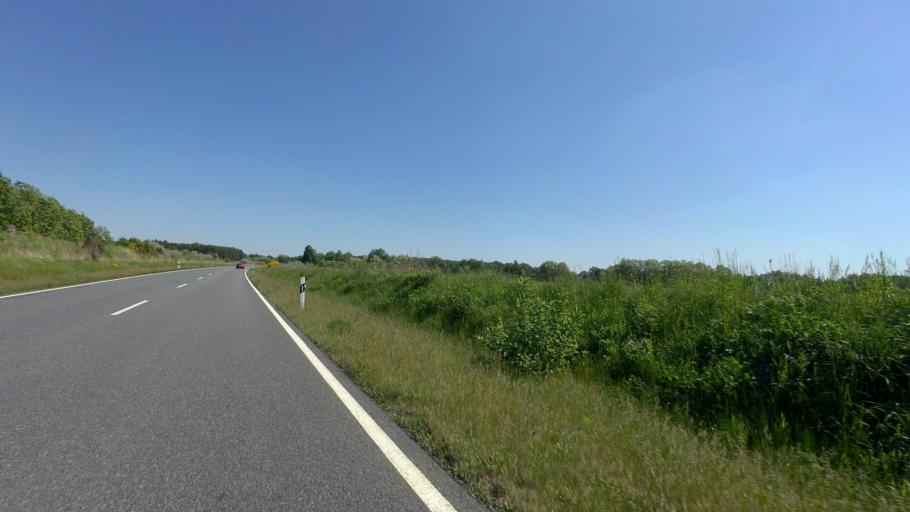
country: DE
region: Brandenburg
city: Spremberg
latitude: 51.5722
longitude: 14.3352
